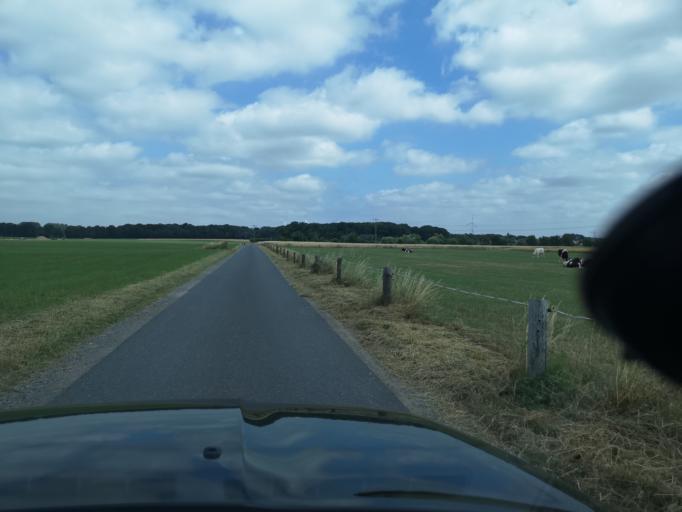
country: DE
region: North Rhine-Westphalia
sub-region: Regierungsbezirk Munster
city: Rhede
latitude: 51.8460
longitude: 6.6810
